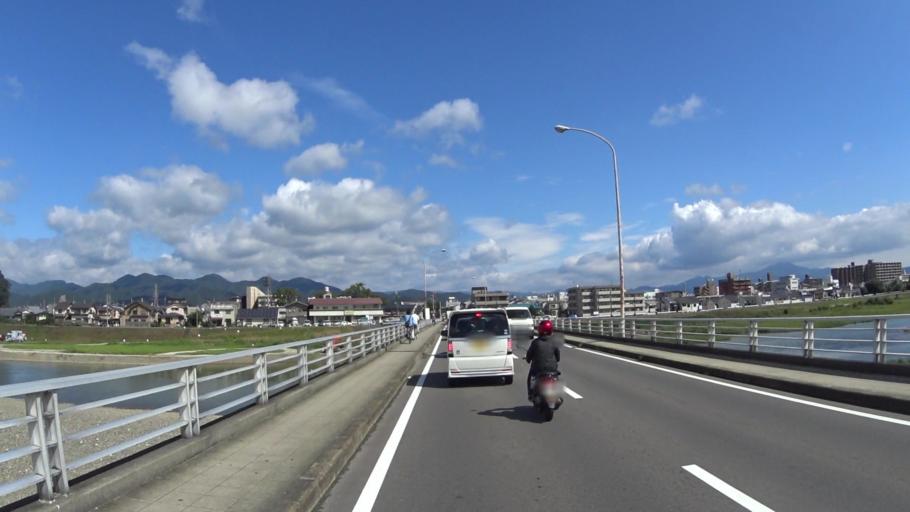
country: JP
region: Kyoto
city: Muko
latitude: 34.9983
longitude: 135.7042
